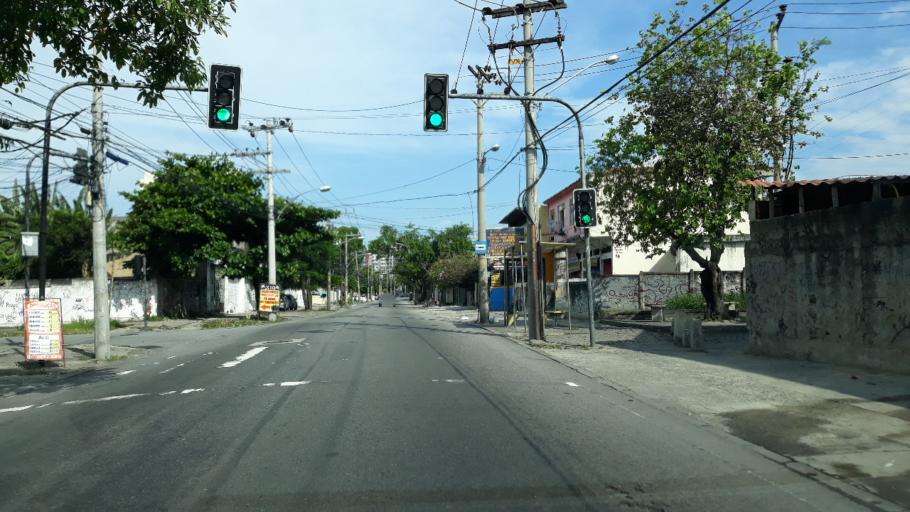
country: BR
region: Rio de Janeiro
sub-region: Duque De Caxias
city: Duque de Caxias
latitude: -22.8411
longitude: -43.2744
